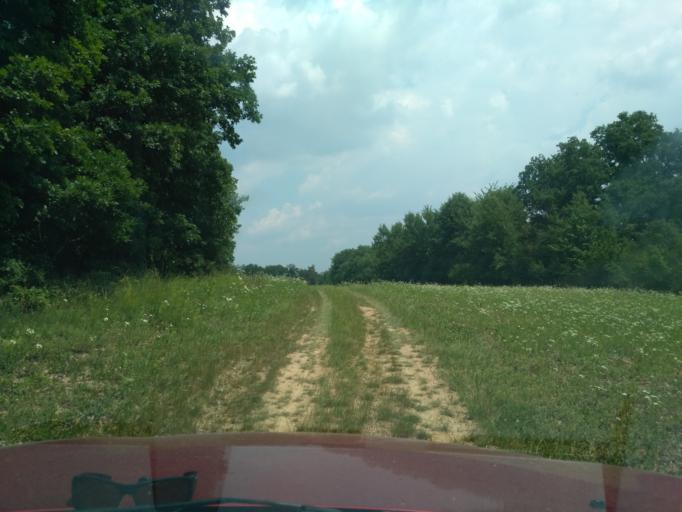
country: SK
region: Kosicky
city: Moldava nad Bodvou
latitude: 48.6297
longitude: 21.0429
